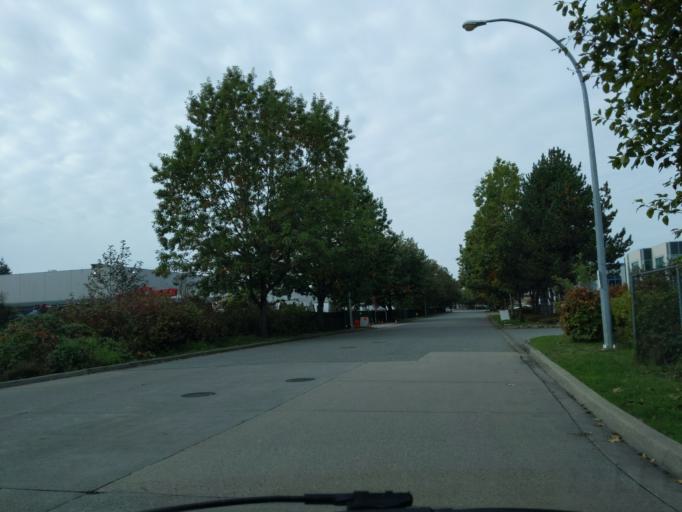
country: CA
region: British Columbia
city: Walnut Grove
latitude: 49.1848
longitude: -122.6597
